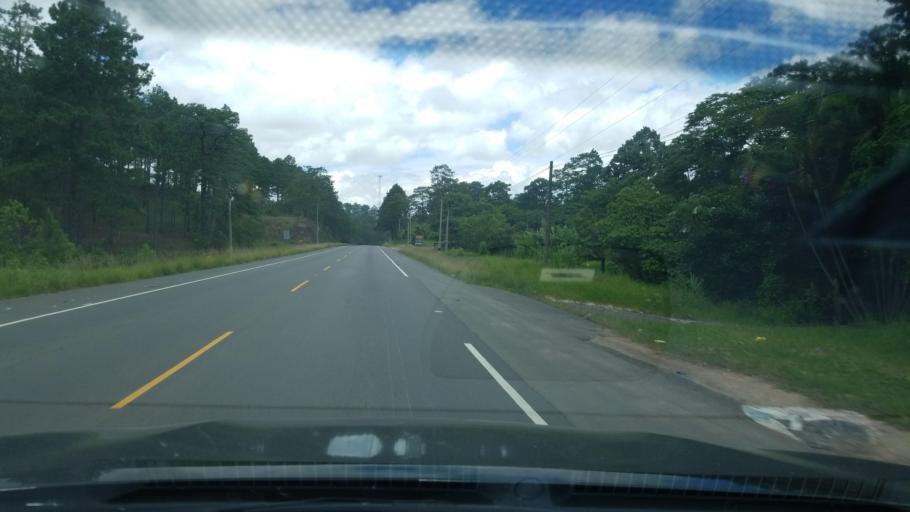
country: HN
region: Francisco Morazan
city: Talanga
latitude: 14.3564
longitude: -87.1516
